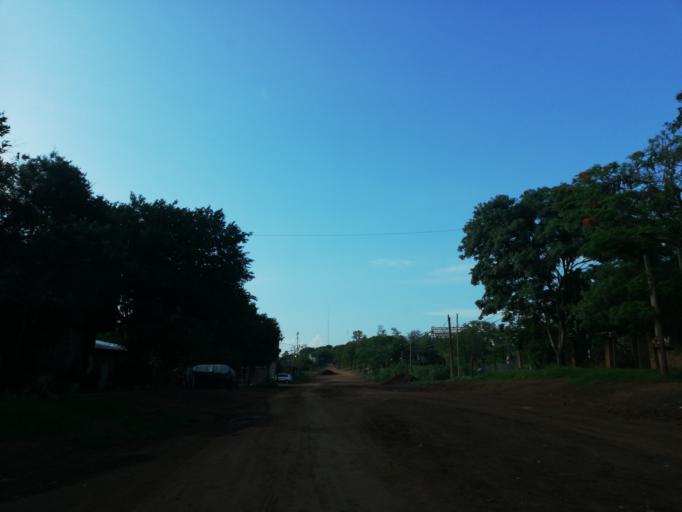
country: AR
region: Misiones
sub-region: Departamento de Capital
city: Posadas
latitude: -27.3971
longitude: -55.9244
